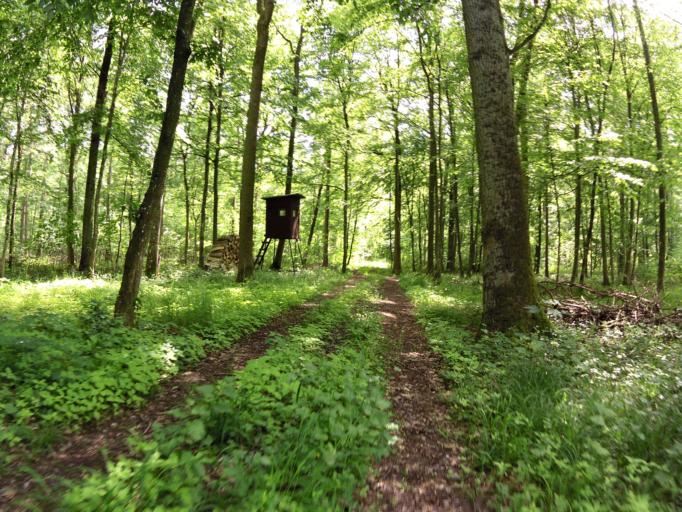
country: DE
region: Bavaria
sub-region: Regierungsbezirk Unterfranken
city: Theilheim
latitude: 49.7311
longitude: 10.0625
